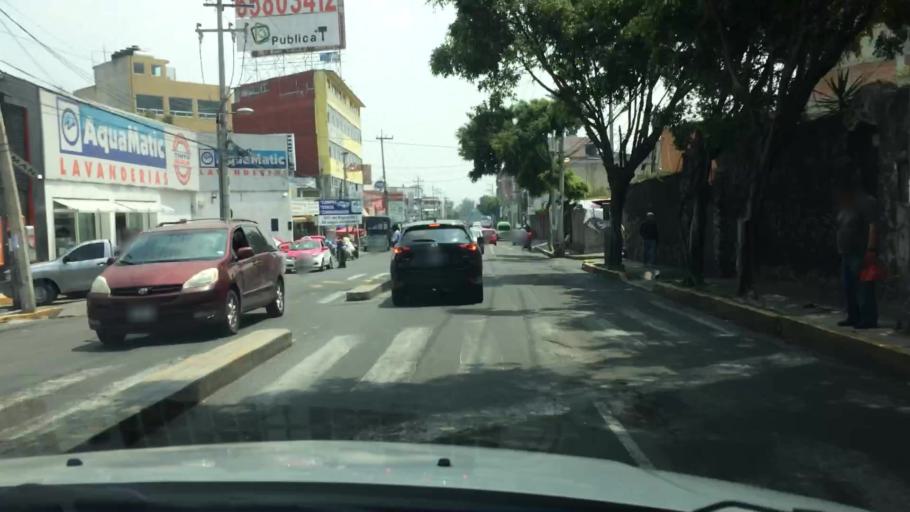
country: MX
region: Mexico City
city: Tlalpan
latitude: 19.3063
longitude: -99.1620
